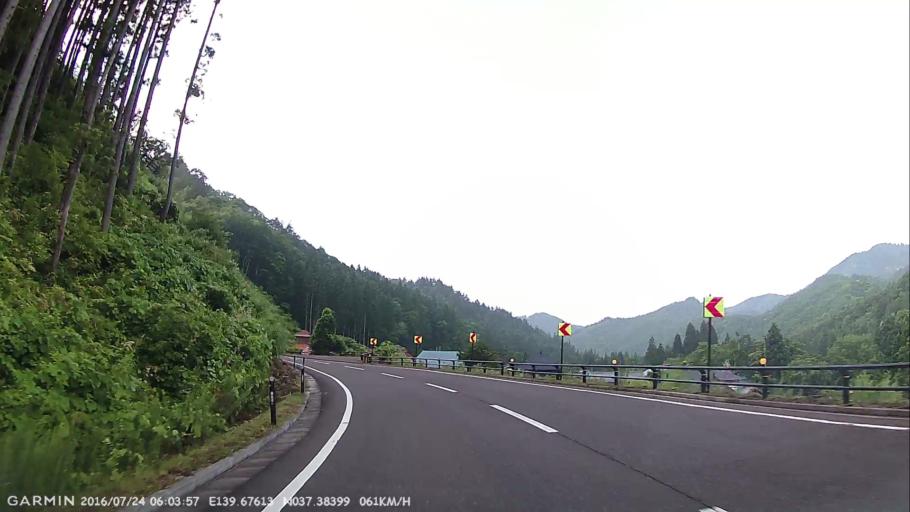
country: JP
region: Fukushima
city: Kitakata
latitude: 37.3840
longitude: 139.6763
